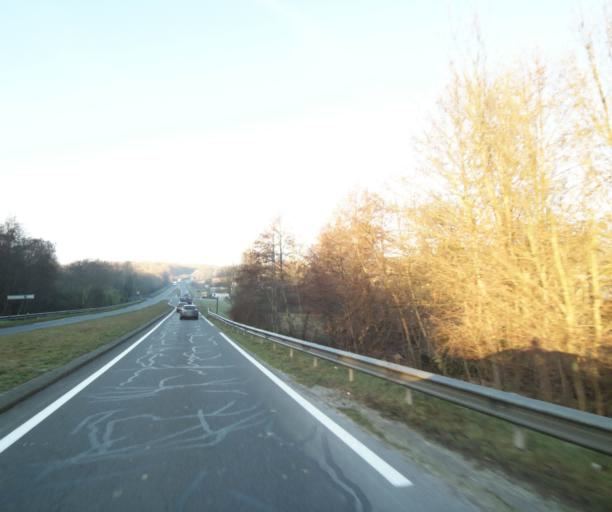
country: FR
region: Poitou-Charentes
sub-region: Departement de la Charente-Maritime
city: Chaniers
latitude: 45.7279
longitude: -0.5141
